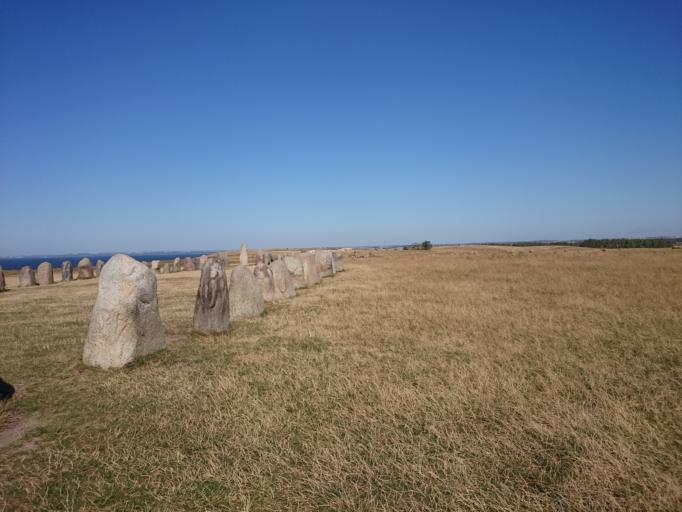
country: SE
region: Skane
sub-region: Ystads Kommun
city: Kopingebro
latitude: 55.3825
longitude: 14.0549
